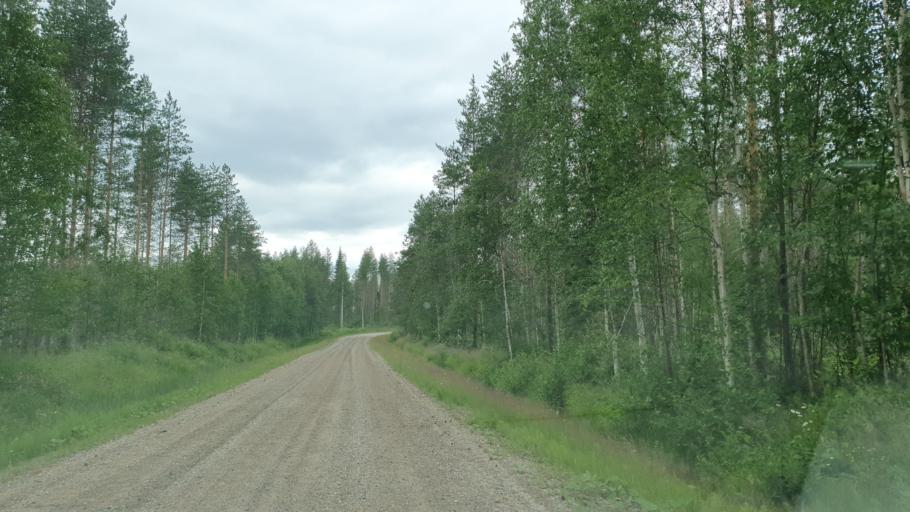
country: FI
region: Kainuu
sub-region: Kehys-Kainuu
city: Kuhmo
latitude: 64.0113
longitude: 29.3411
